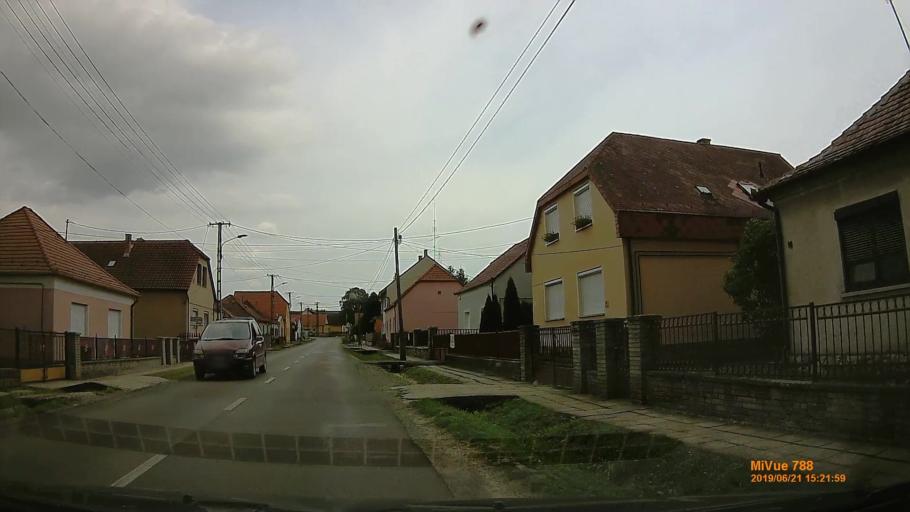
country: HU
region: Baranya
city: Pecs
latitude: 46.0442
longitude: 18.2490
